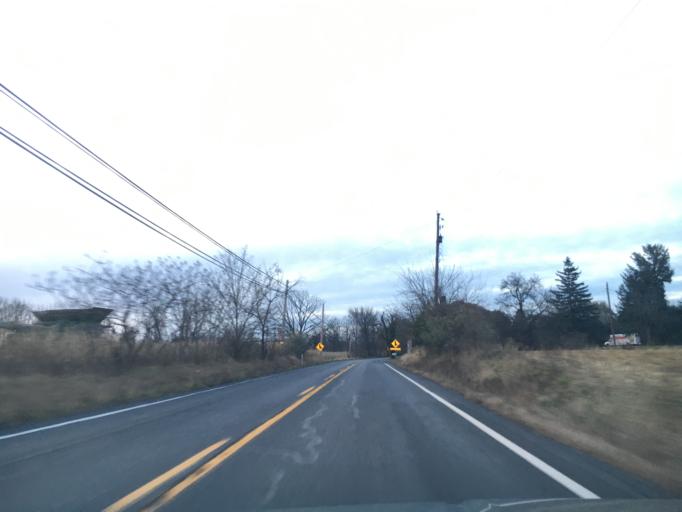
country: US
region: Pennsylvania
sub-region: Lehigh County
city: Stiles
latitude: 40.6476
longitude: -75.5321
